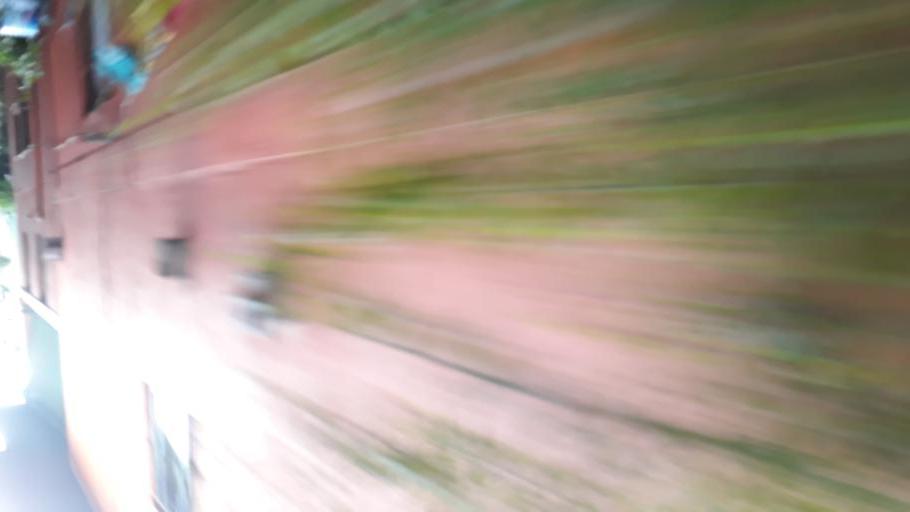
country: LK
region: Western
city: Colombo
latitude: 6.9257
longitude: 79.8488
